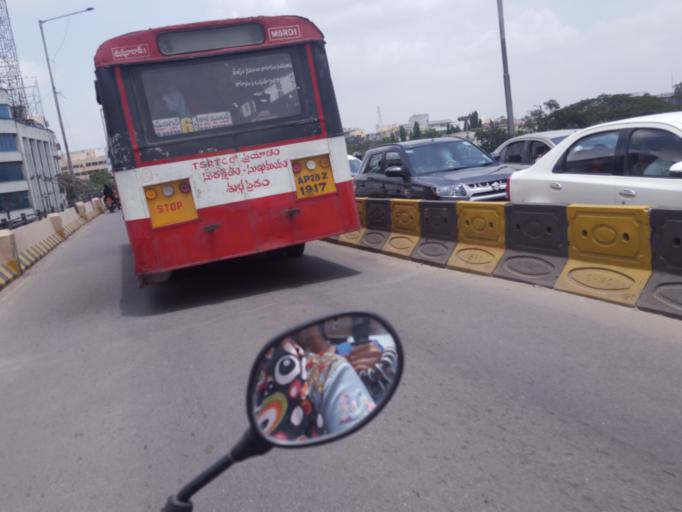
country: IN
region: Telangana
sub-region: Hyderabad
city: Hyderabad
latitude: 17.4031
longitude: 78.4524
